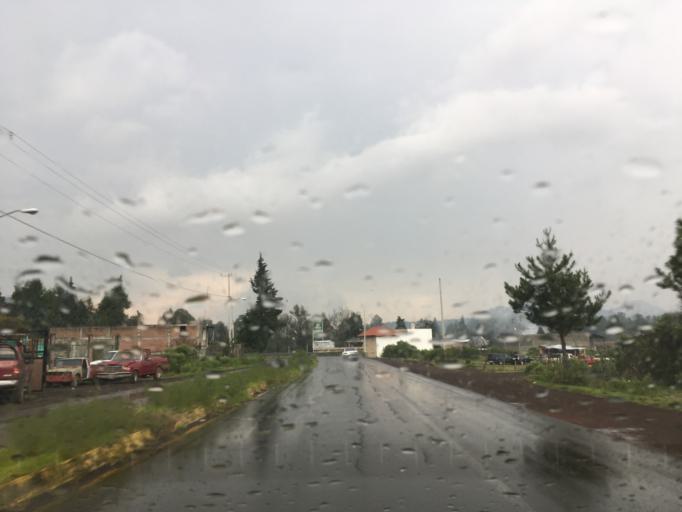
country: MX
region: Michoacan
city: Angahuan
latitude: 19.5496
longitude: -102.2173
